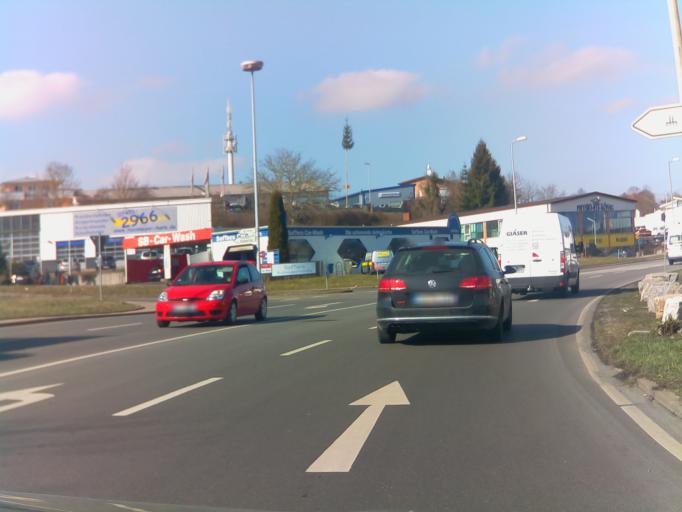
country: DE
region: Baden-Wuerttemberg
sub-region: Karlsruhe Region
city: Horb am Neckar
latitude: 48.4557
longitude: 8.6999
